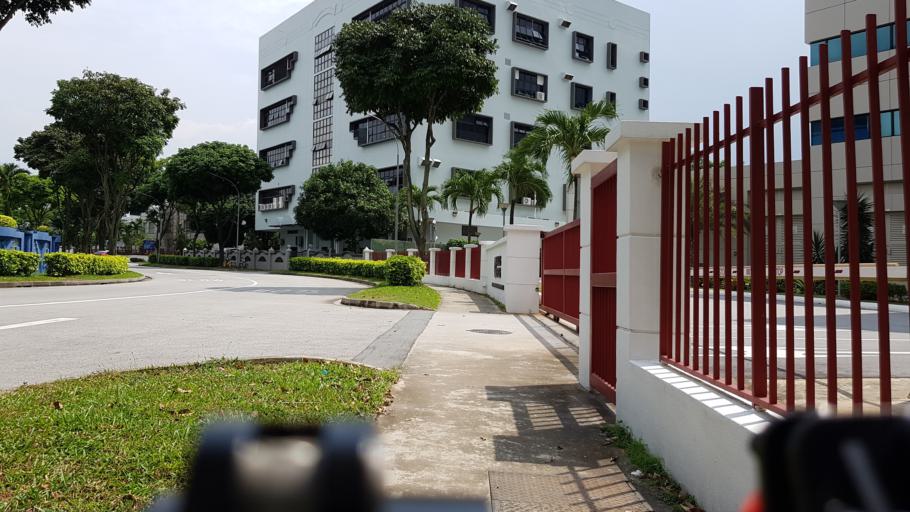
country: MY
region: Johor
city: Kampung Pasir Gudang Baru
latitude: 1.4423
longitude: 103.8374
